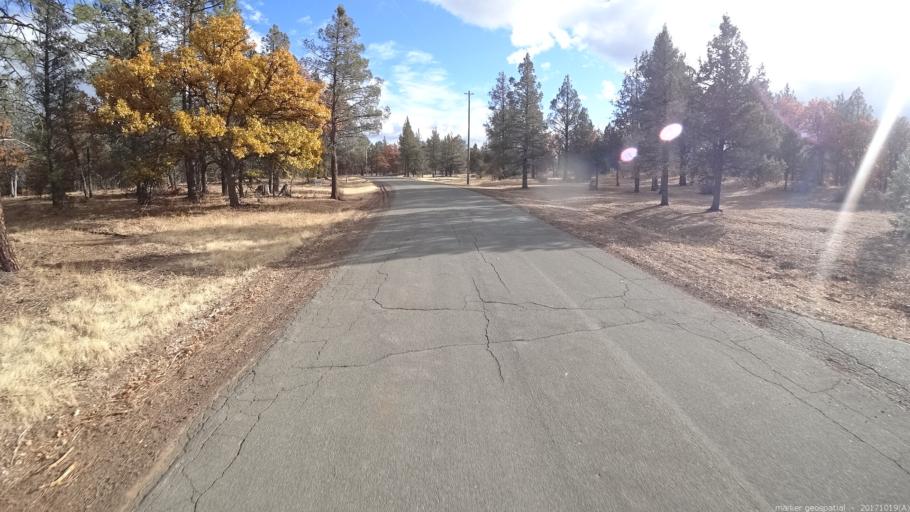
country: US
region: California
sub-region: Shasta County
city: Burney
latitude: 40.9732
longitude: -121.4444
